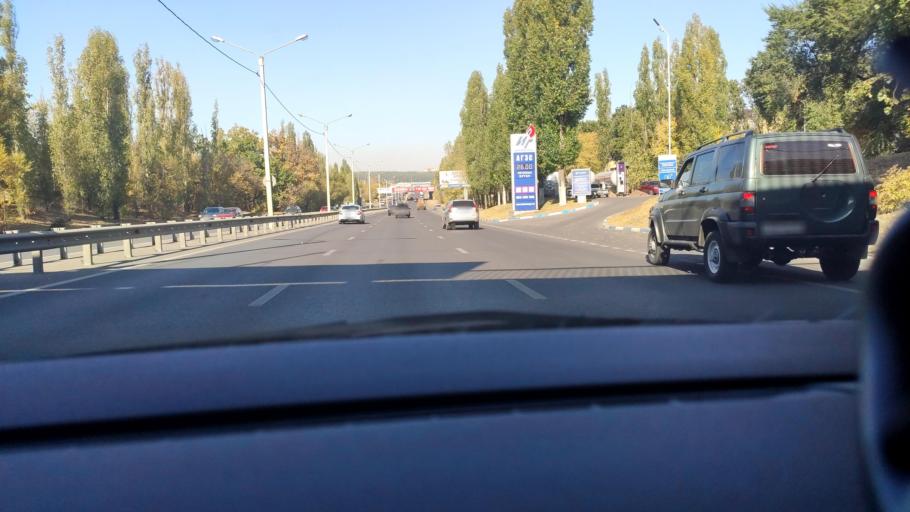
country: RU
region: Voronezj
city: Voronezh
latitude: 51.6614
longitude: 39.1308
